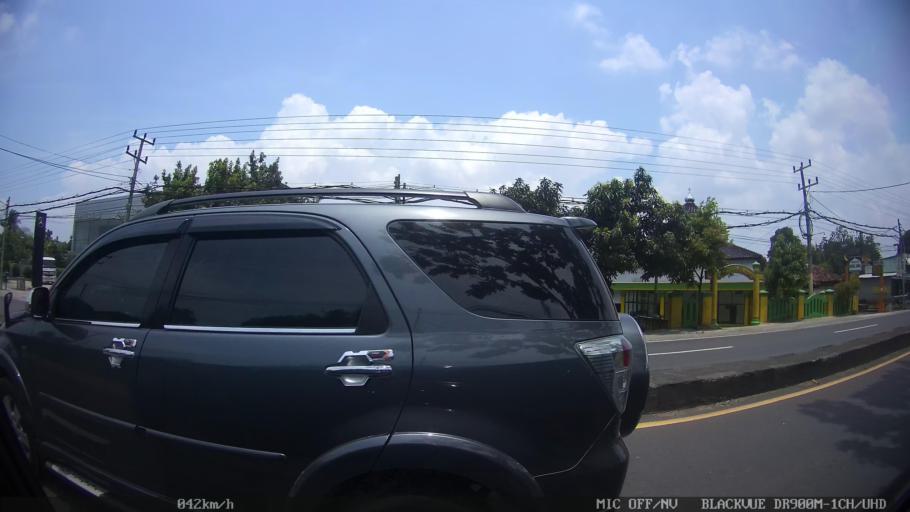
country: ID
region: Lampung
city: Natar
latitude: -5.3444
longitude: 105.2148
